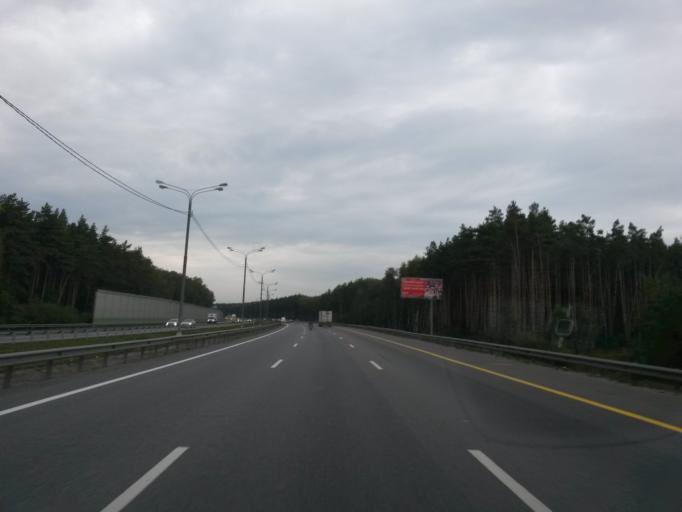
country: RU
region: Moskovskaya
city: Domodedovo
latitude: 55.4439
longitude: 37.7974
